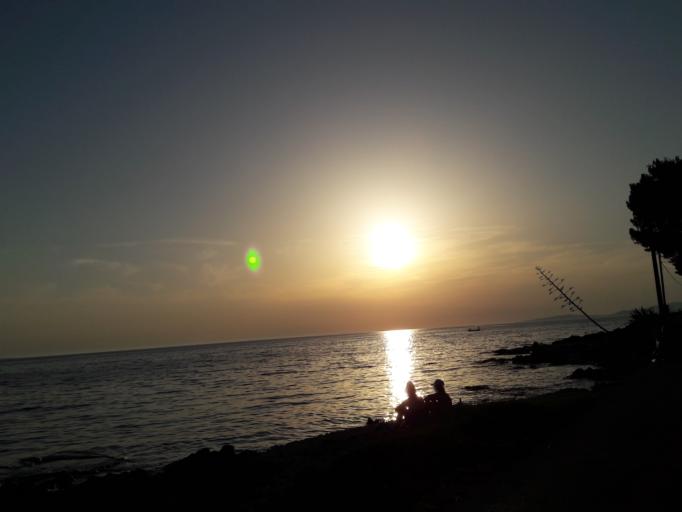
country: HR
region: Licko-Senjska
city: Novalja
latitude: 44.3702
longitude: 14.6936
